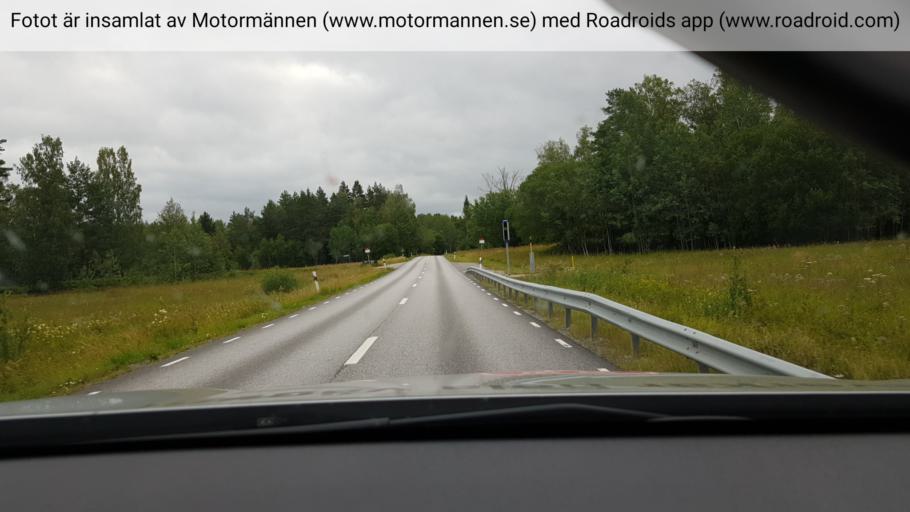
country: SE
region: Stockholm
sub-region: Norrtalje Kommun
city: Skanninge
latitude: 59.8725
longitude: 18.4704
